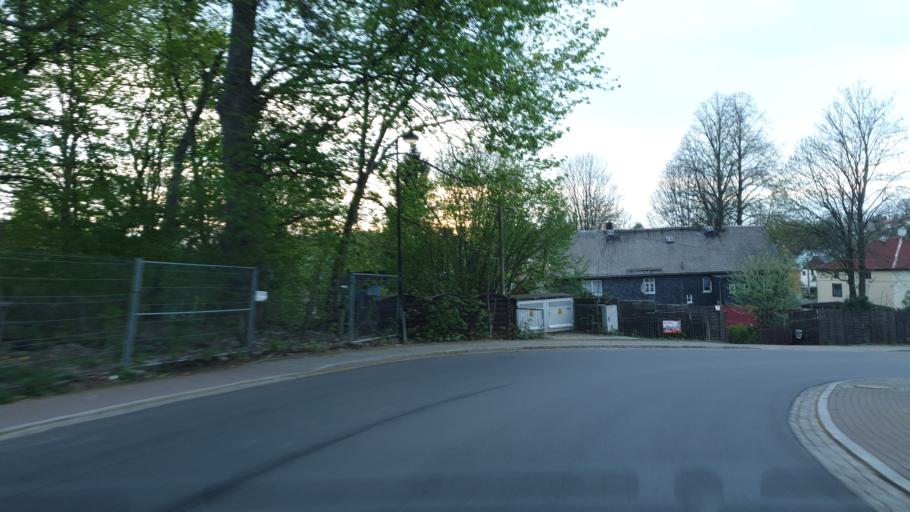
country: DE
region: Saxony
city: Gersdorf
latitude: 50.7463
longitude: 12.7224
